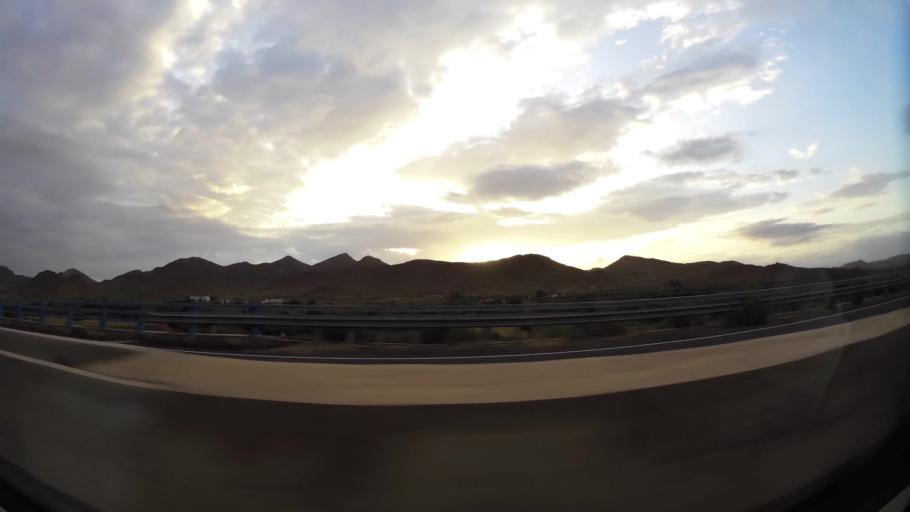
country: MA
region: Oriental
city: Taourirt
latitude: 34.4795
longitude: -2.9858
